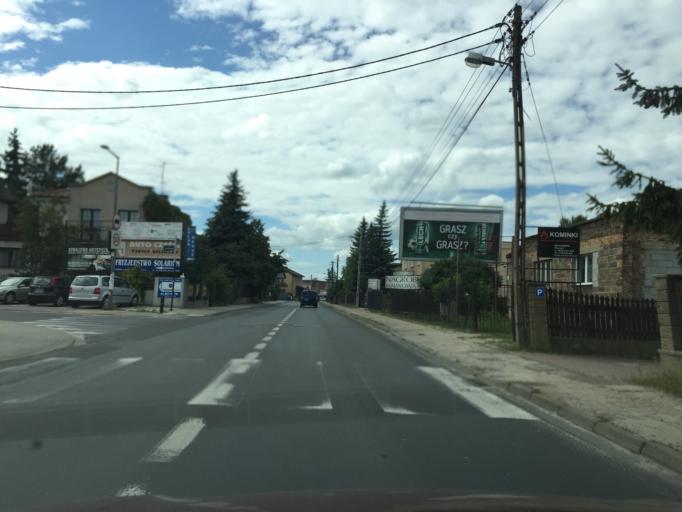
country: PL
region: Greater Poland Voivodeship
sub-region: Powiat poznanski
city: Plewiska
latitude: 52.3854
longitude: 16.8227
